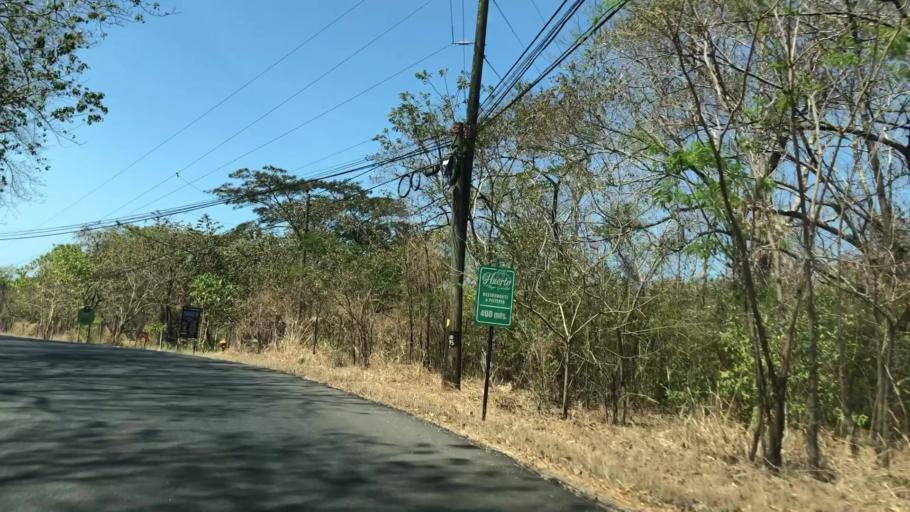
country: CR
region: Guanacaste
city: Sardinal
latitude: 10.3454
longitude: -85.8421
